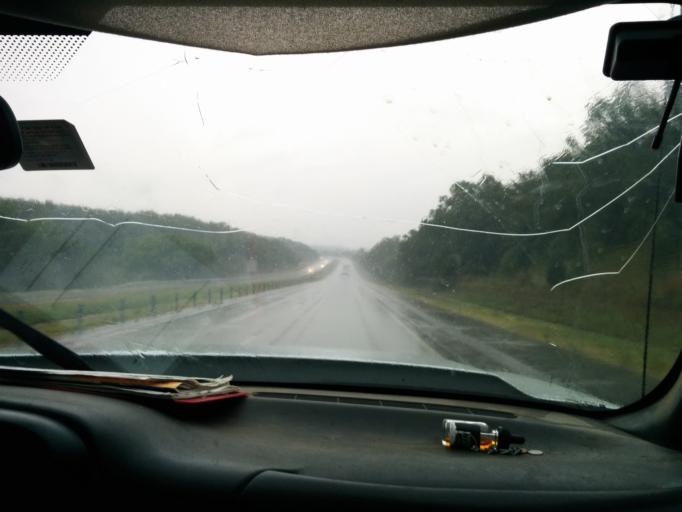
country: US
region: Oklahoma
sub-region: Okmulgee County
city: Beggs
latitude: 35.7259
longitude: -96.0011
